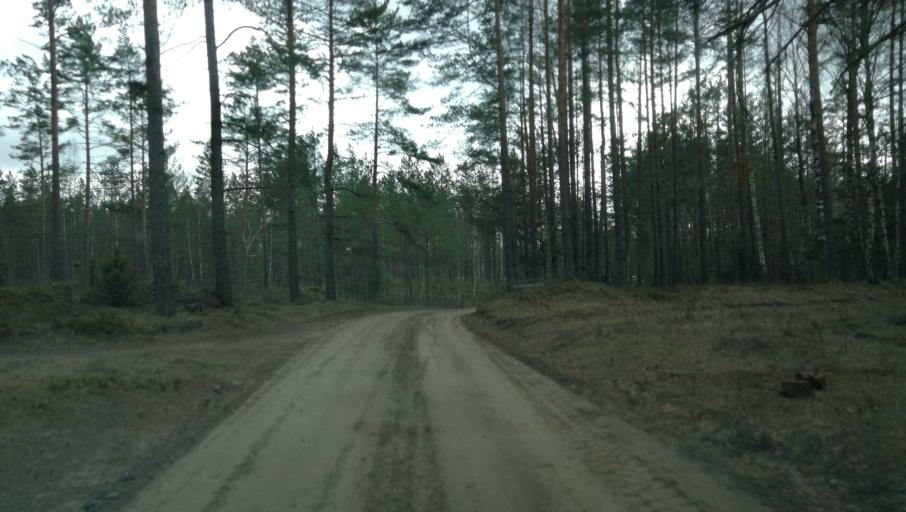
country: LV
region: Adazi
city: Adazi
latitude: 57.0627
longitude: 24.2629
